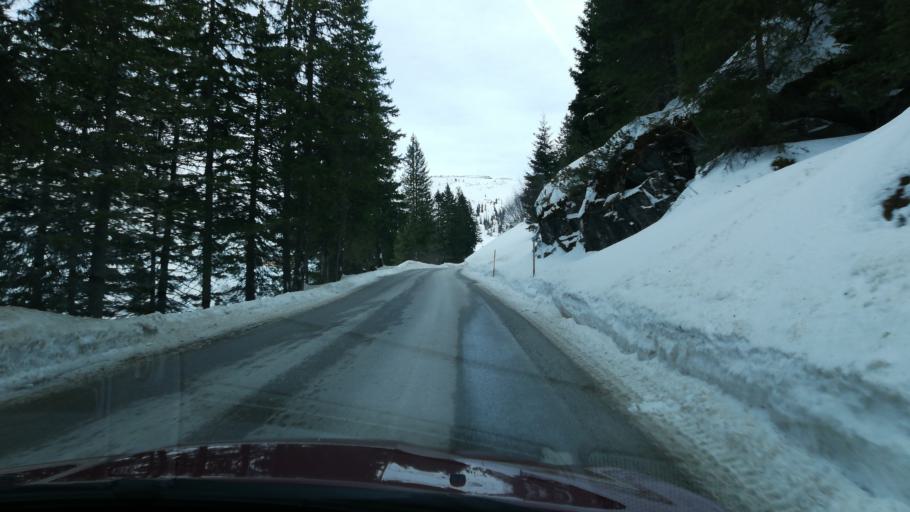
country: AT
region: Styria
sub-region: Politischer Bezirk Liezen
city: Donnersbach
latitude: 47.4073
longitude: 14.1922
